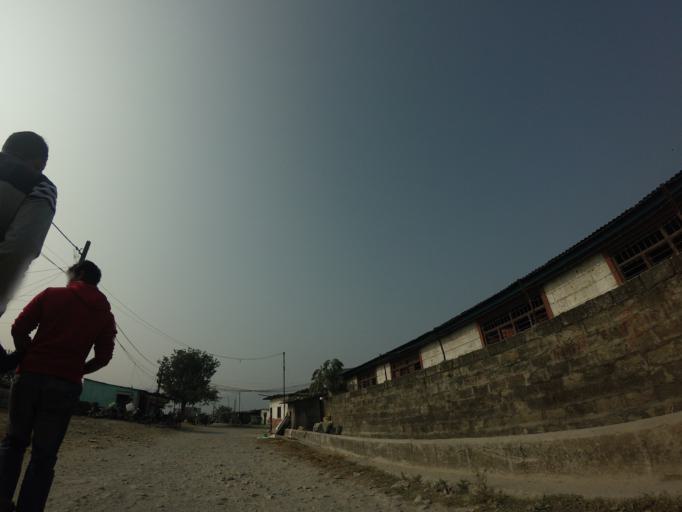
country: NP
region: Western Region
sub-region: Gandaki Zone
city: Pokhara
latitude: 28.2065
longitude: 83.9881
